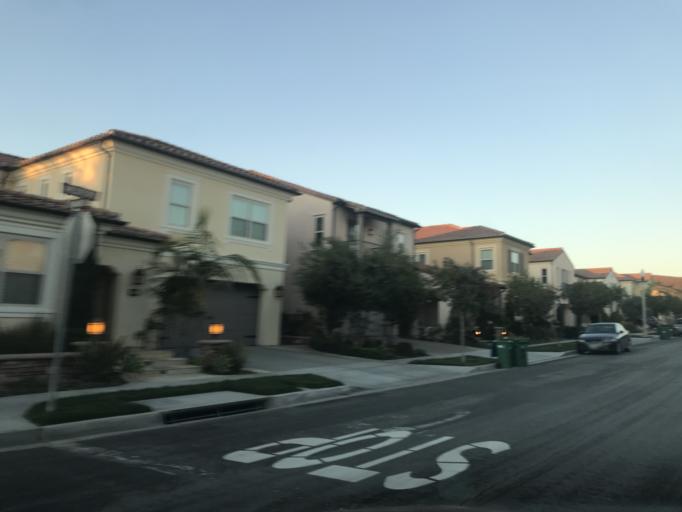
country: US
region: California
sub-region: Orange County
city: Lake Forest
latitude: 33.7054
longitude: -117.7381
